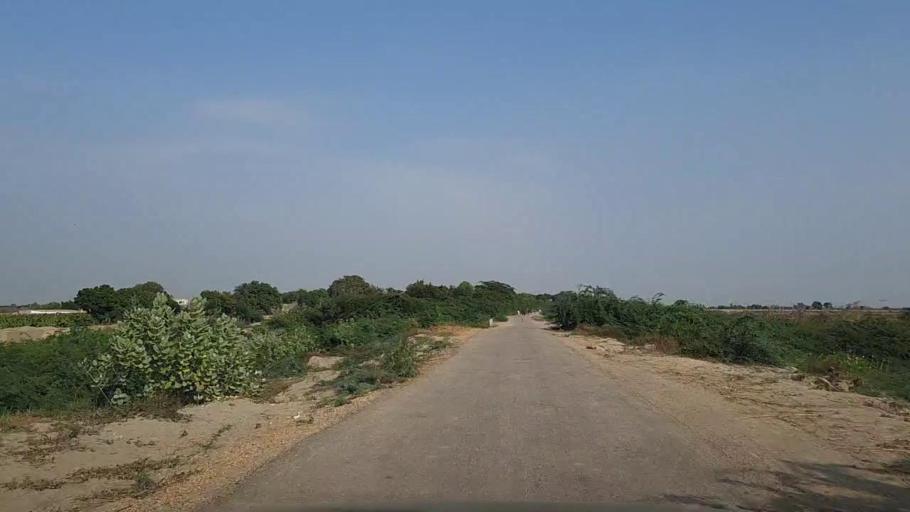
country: PK
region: Sindh
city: Thatta
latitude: 24.6518
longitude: 67.9150
